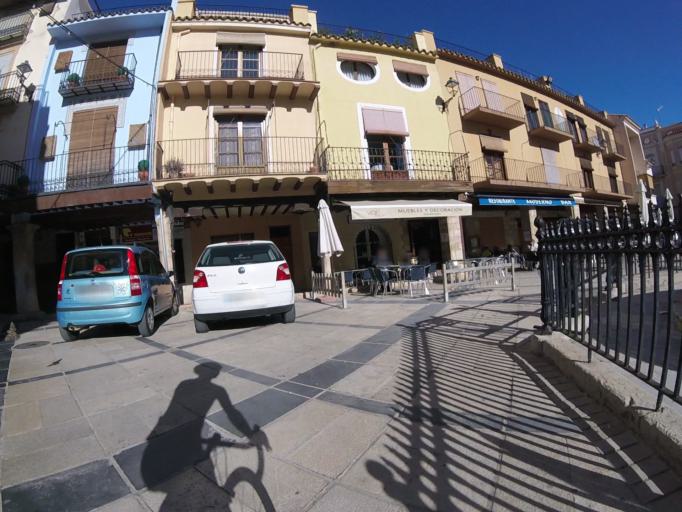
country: ES
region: Valencia
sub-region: Provincia de Castello
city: Chert/Xert
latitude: 40.4654
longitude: 0.1799
